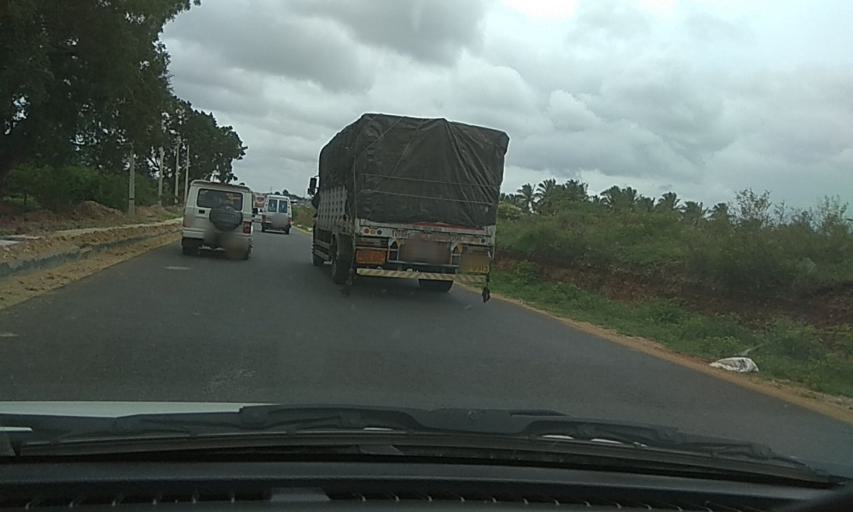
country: IN
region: Karnataka
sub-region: Chitradurga
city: Chitradurga
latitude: 14.2913
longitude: 76.2856
